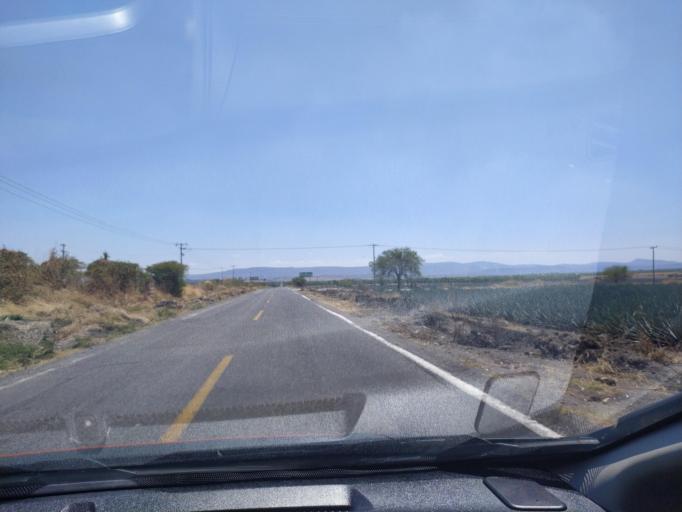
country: MX
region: Guanajuato
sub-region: San Francisco del Rincon
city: San Ignacio de Hidalgo
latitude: 20.7883
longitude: -101.8357
